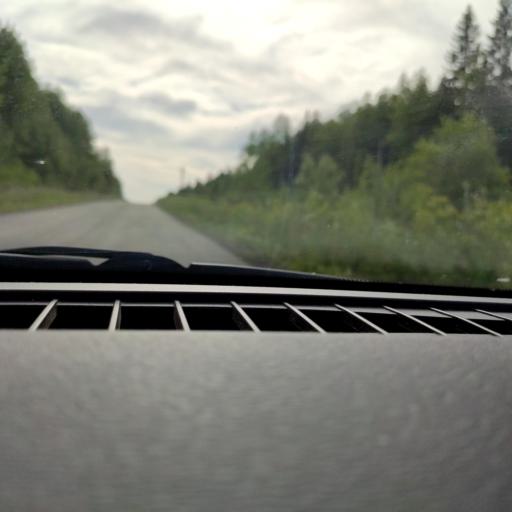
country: RU
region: Perm
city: Polazna
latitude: 58.3351
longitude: 56.1628
